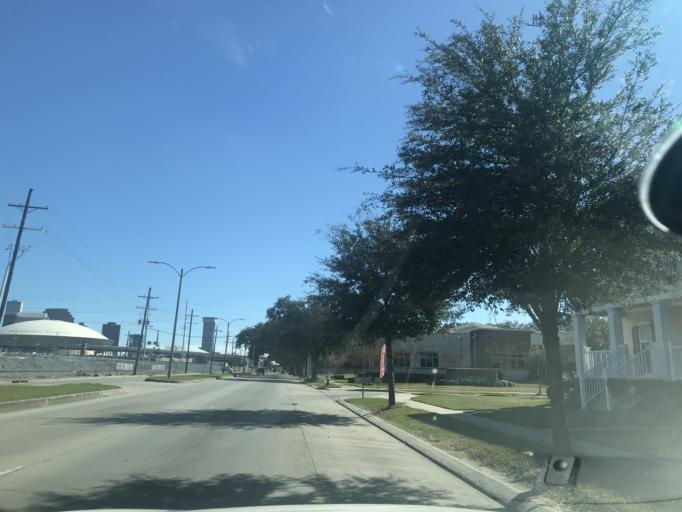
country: US
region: Louisiana
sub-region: Orleans Parish
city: New Orleans
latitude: 29.9532
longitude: -90.0932
